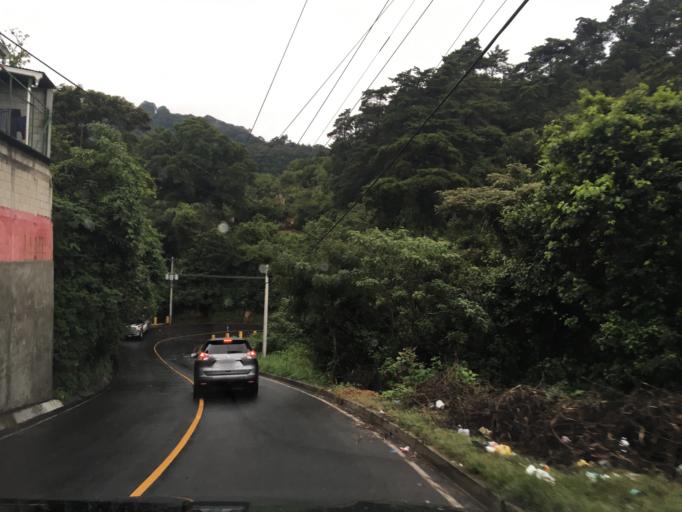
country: GT
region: Guatemala
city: Santa Catarina Pinula
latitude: 14.5527
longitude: -90.5056
